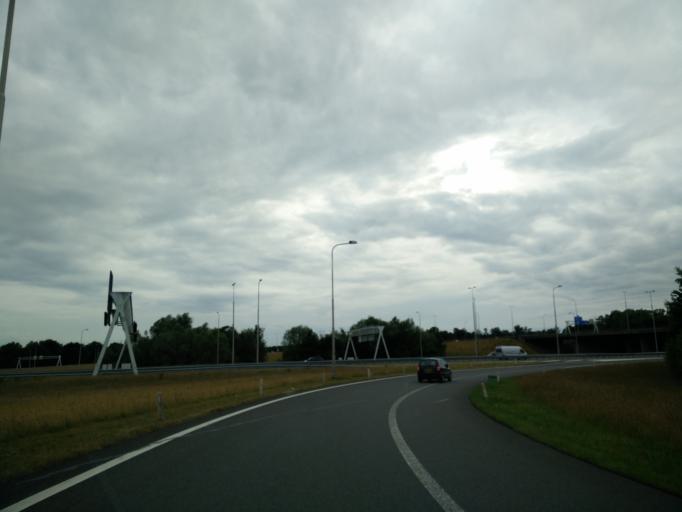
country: NL
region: Gelderland
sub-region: Gemeente Apeldoorn
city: Apeldoorn
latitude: 52.1868
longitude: 6.0250
